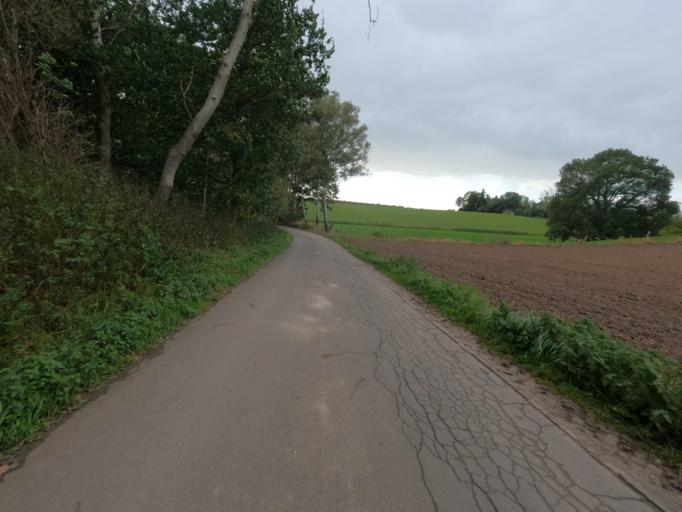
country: DE
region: North Rhine-Westphalia
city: Huckelhoven
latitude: 51.0538
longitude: 6.2731
